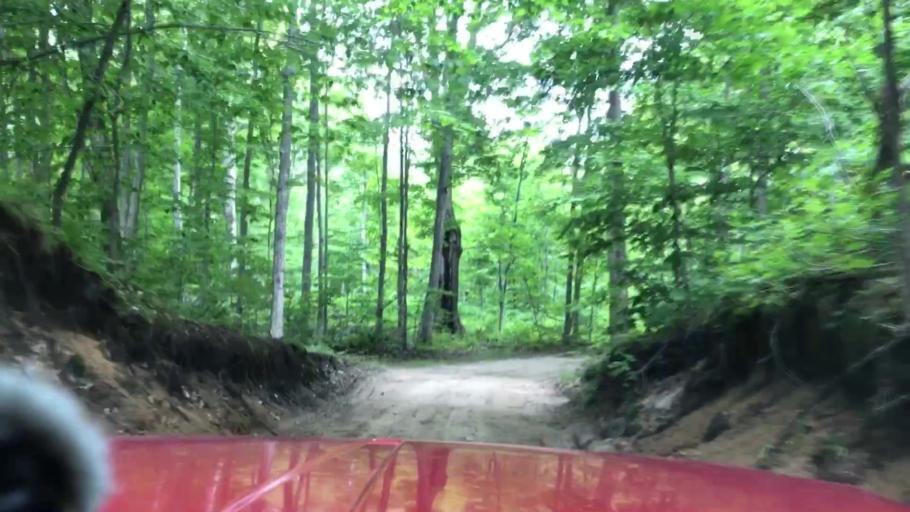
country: US
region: Michigan
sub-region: Charlevoix County
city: Charlevoix
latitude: 45.7221
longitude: -85.5640
